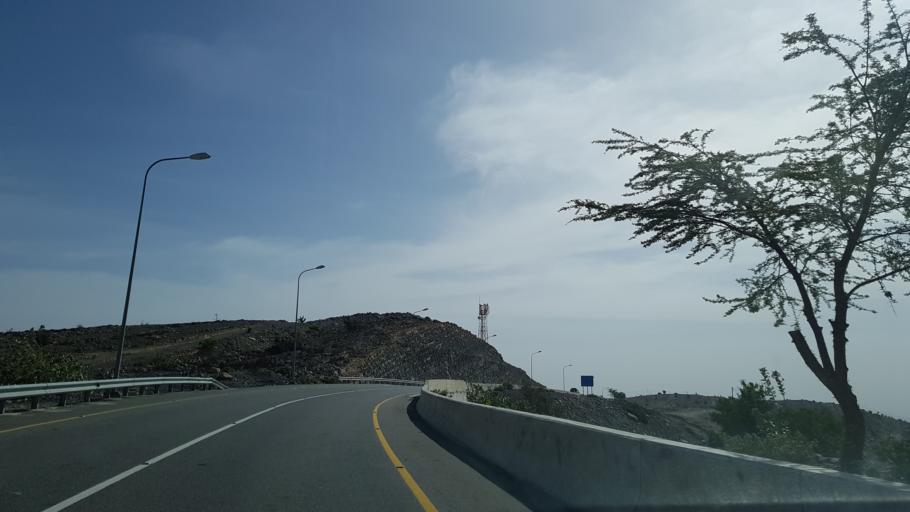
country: OM
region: Muhafazat ad Dakhiliyah
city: Izki
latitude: 23.0260
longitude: 57.6985
